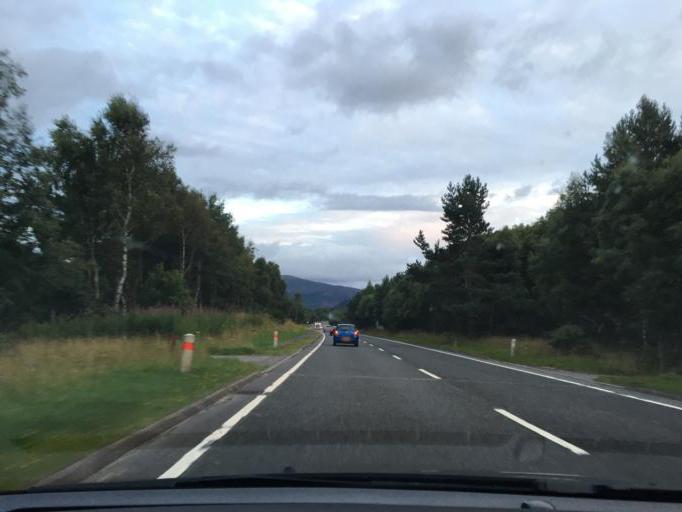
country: GB
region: Scotland
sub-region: Highland
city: Aviemore
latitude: 57.1889
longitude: -3.8367
